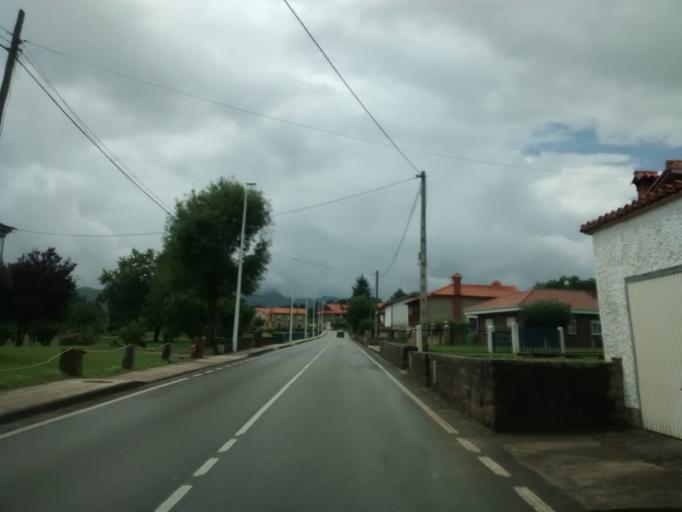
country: ES
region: Cantabria
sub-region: Provincia de Cantabria
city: Entrambasaguas
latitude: 43.3655
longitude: -3.6989
